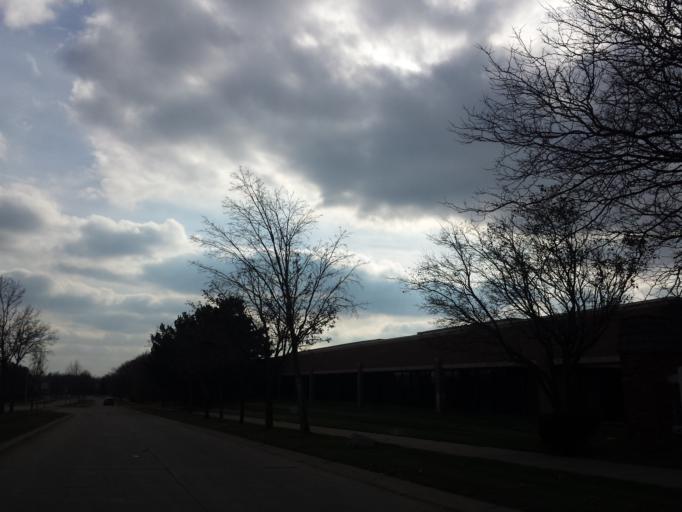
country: US
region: Michigan
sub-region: Wayne County
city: Plymouth
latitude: 42.4104
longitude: -83.4288
